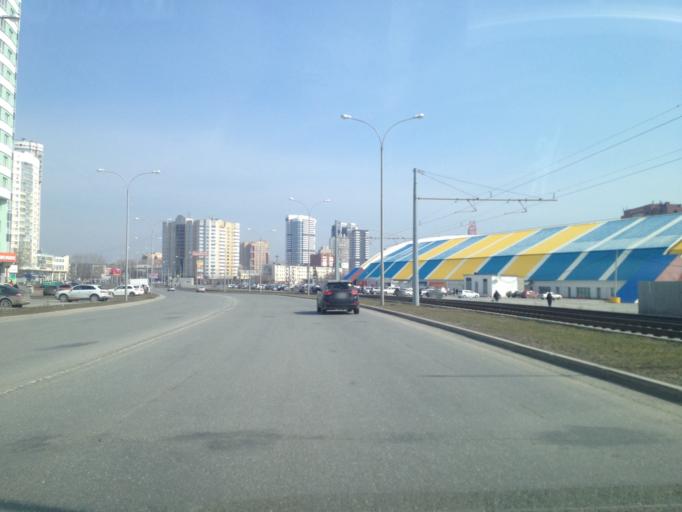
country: RU
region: Sverdlovsk
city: Yekaterinburg
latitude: 56.7976
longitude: 60.6235
